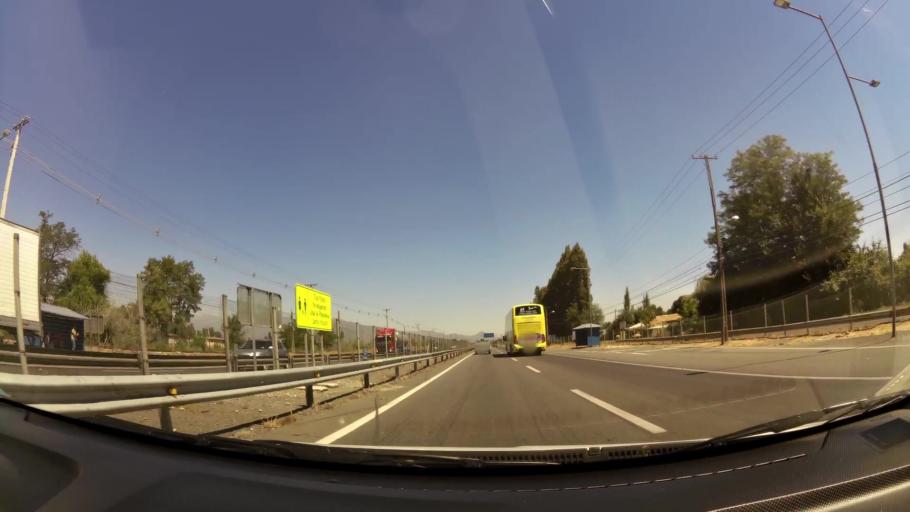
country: CL
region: O'Higgins
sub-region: Provincia de Cachapoal
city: Rengo
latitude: -34.3241
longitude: -70.8313
